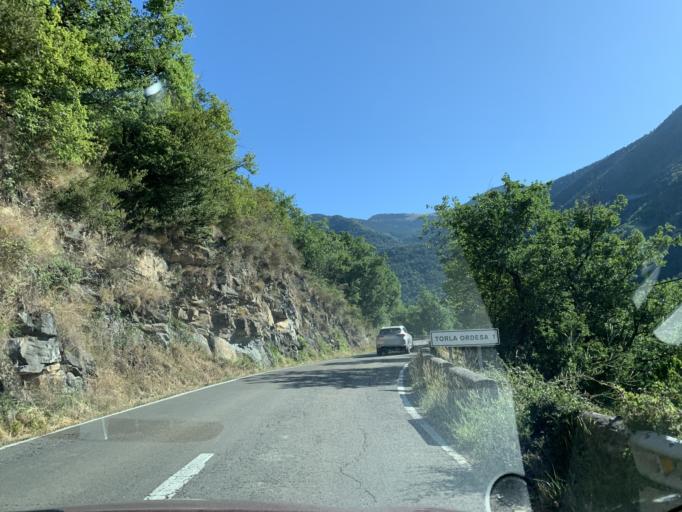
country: ES
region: Aragon
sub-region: Provincia de Huesca
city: Broto
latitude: 42.6160
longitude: -0.1181
